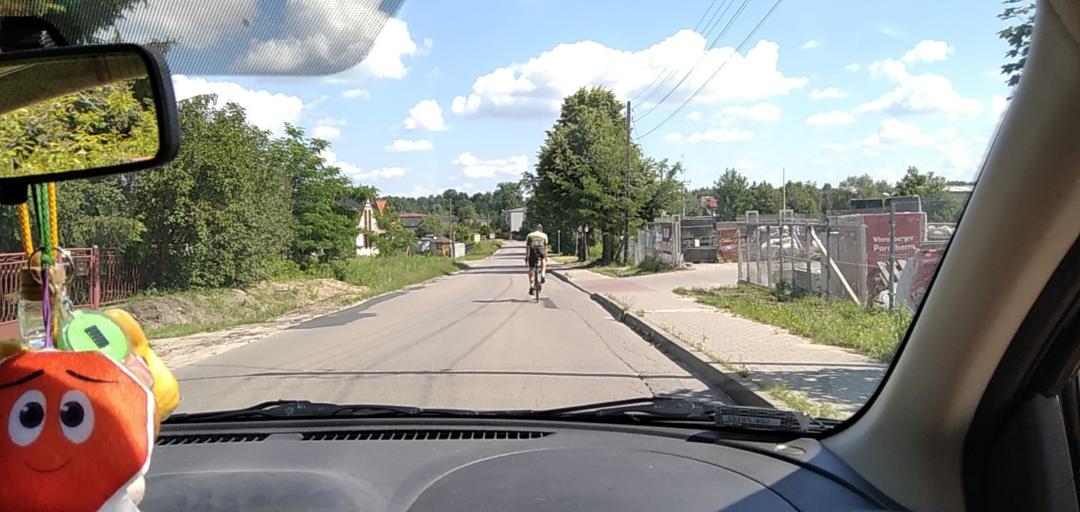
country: PL
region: Silesian Voivodeship
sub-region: Powiat bedzinski
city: Sarnow
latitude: 50.3834
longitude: 19.1367
